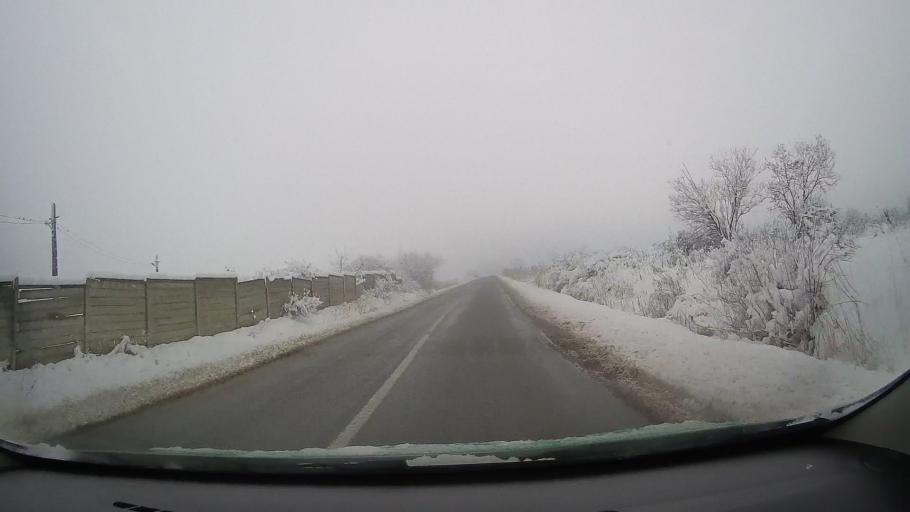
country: RO
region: Sibiu
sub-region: Comuna Orlat
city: Orlat
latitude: 45.7812
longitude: 23.9448
